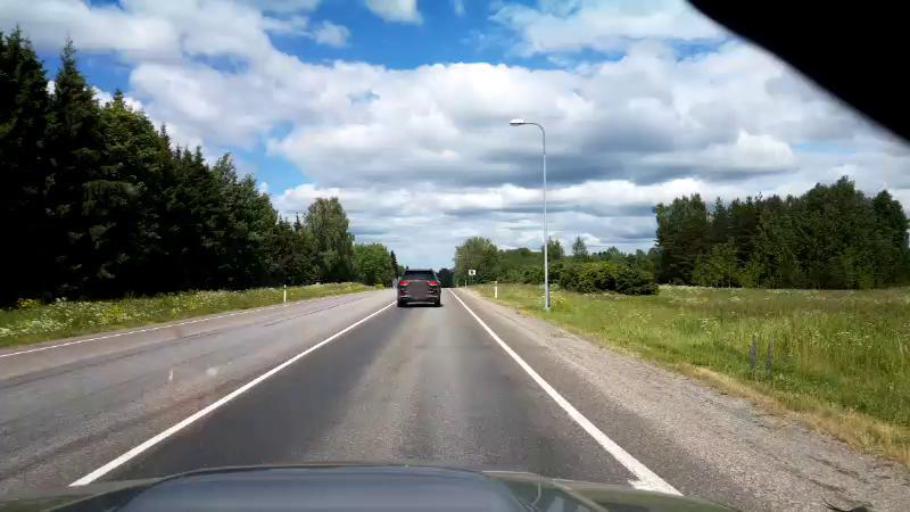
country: EE
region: Harju
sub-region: Keila linn
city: Keila
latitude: 59.1402
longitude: 24.5031
